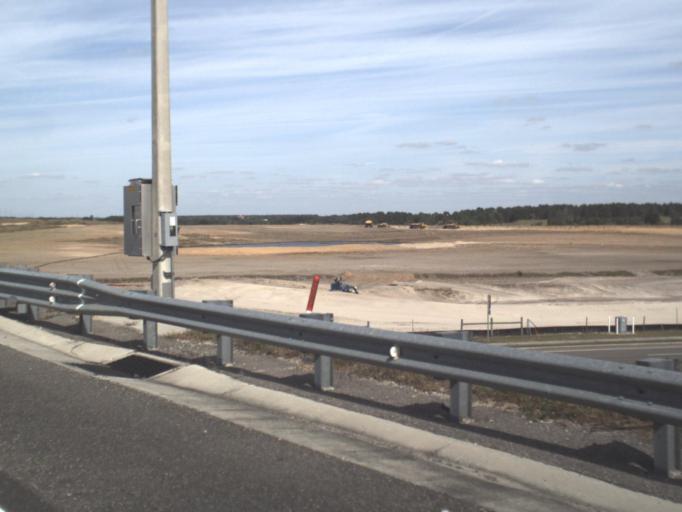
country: US
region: Florida
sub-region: Polk County
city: Citrus Ridge
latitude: 28.4193
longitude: -81.6319
